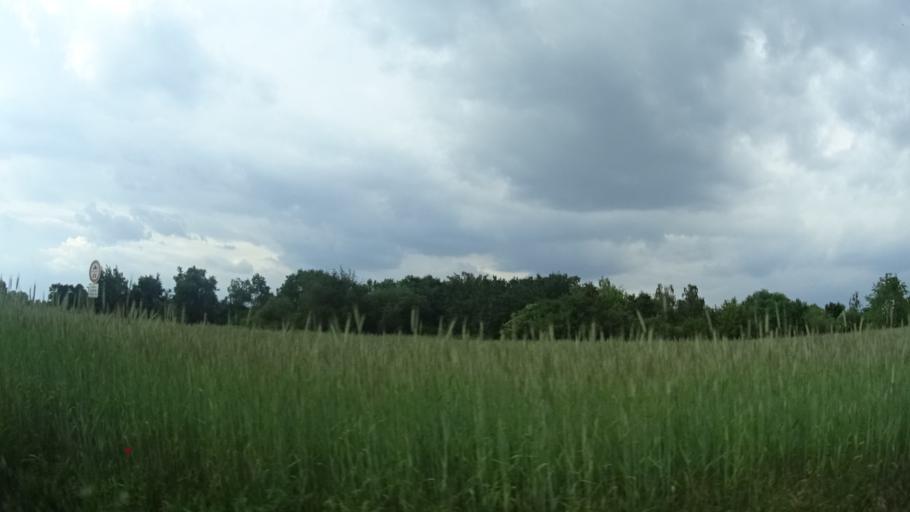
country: DE
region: Rheinland-Pfalz
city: Schifferstadt
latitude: 49.3754
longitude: 8.3653
